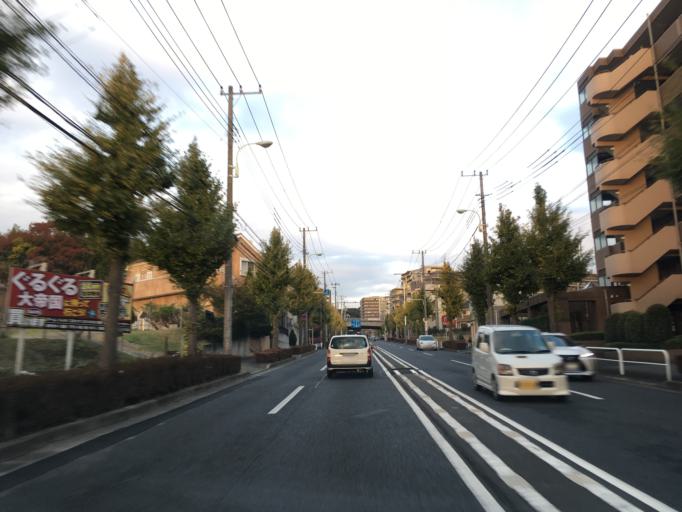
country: JP
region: Tokyo
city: Hachioji
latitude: 35.6004
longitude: 139.3634
